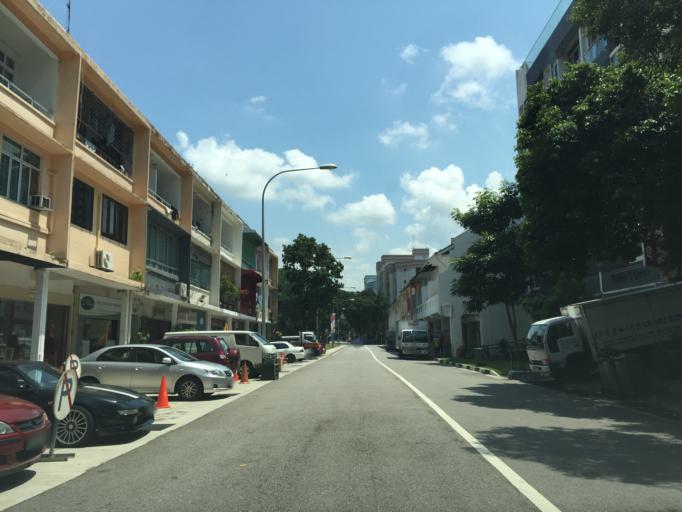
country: SG
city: Singapore
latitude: 1.3137
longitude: 103.8530
